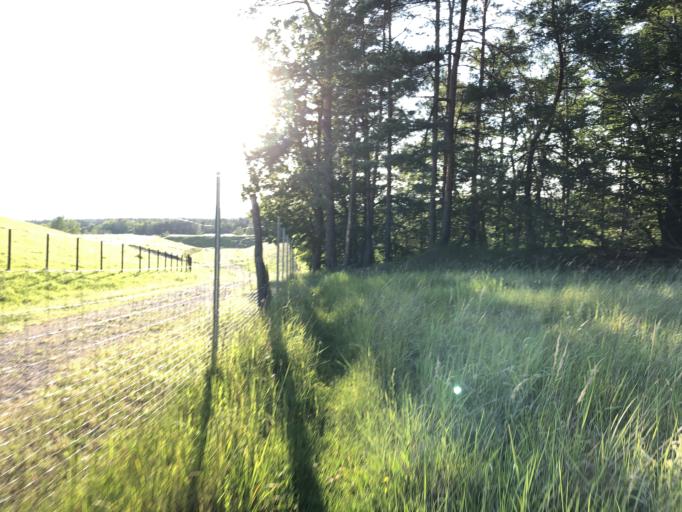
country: DE
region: Bavaria
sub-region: Upper Franconia
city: Memmelsdorf
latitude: 49.9148
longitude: 10.9519
